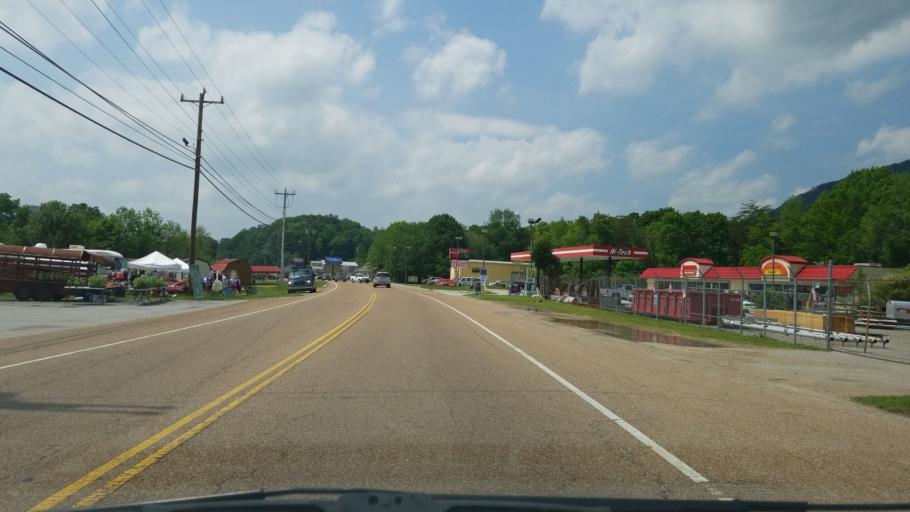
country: US
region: Tennessee
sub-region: Hamilton County
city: Falling Water
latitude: 35.2199
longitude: -85.2244
